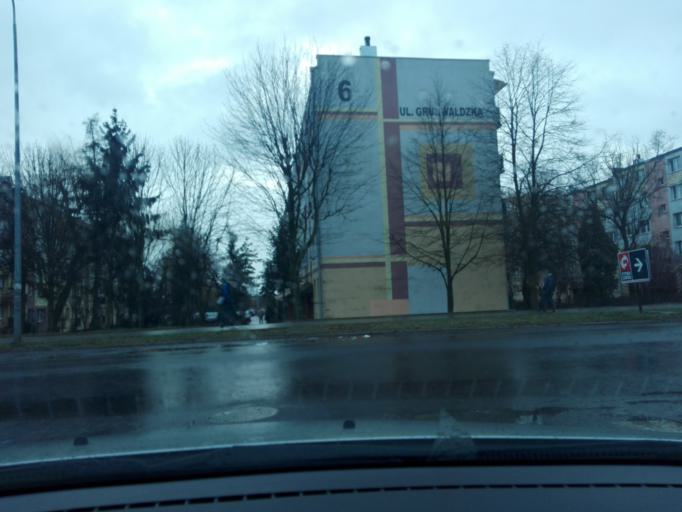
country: PL
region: Lodz Voivodeship
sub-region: Powiat kutnowski
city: Kutno
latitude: 52.2289
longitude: 19.3713
